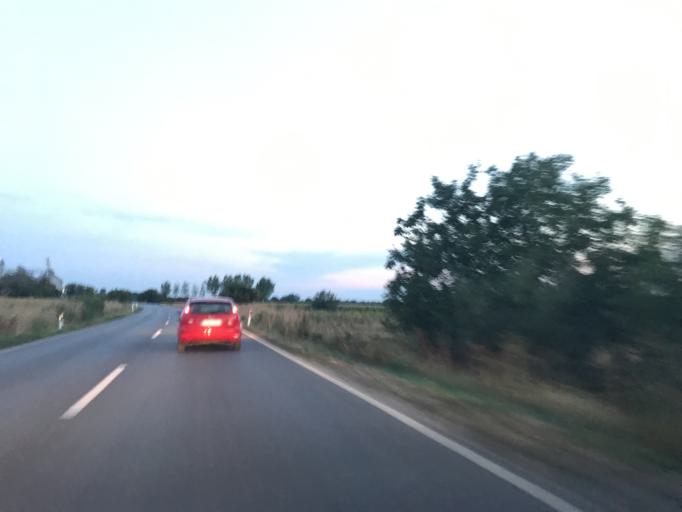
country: RS
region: Central Serbia
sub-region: Branicevski Okrug
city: Pozarevac
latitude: 44.6312
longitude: 21.1449
